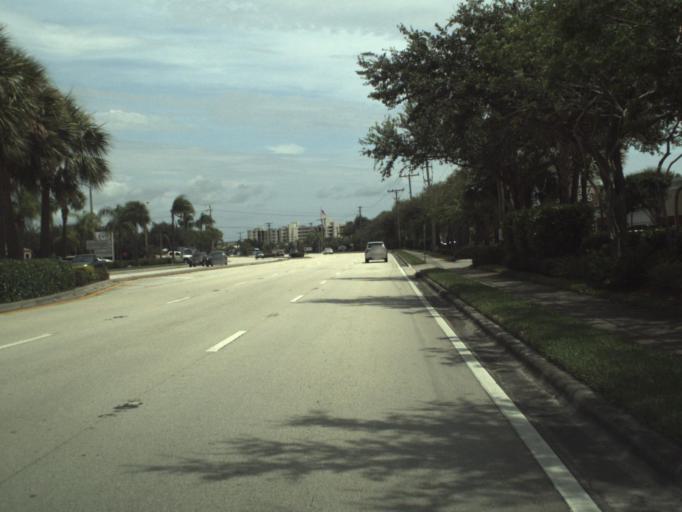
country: US
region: Florida
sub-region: Palm Beach County
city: Jupiter
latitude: 26.9603
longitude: -80.0846
